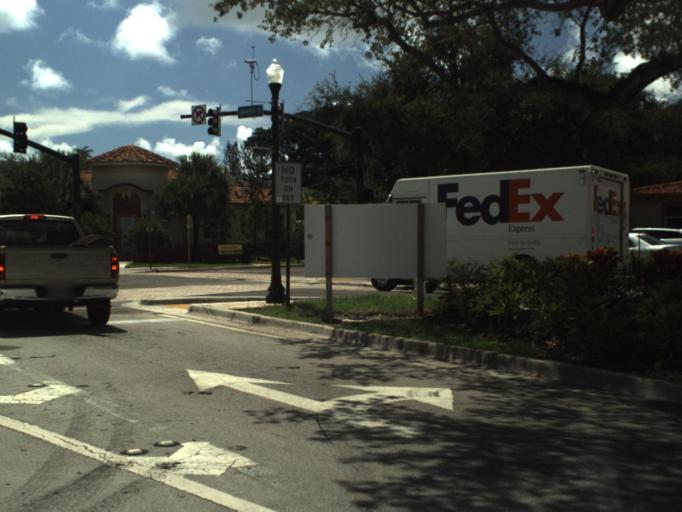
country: US
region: Florida
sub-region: Broward County
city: Hollywood
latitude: 26.0100
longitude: -80.1594
